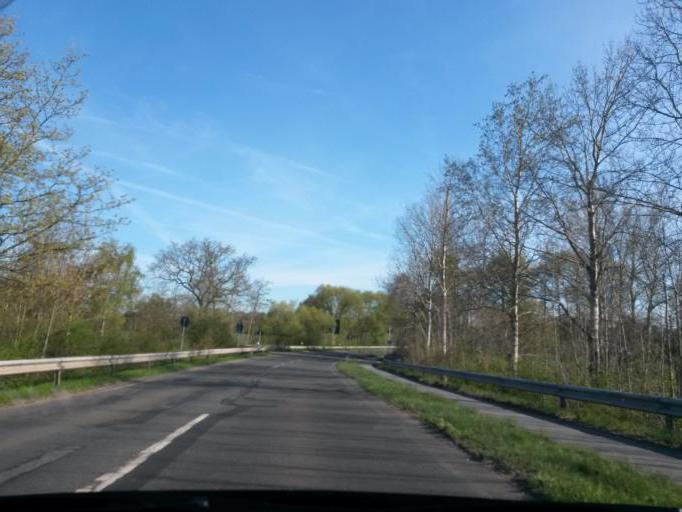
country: DE
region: Schleswig-Holstein
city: Rellingen
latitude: 53.6107
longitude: 9.8148
